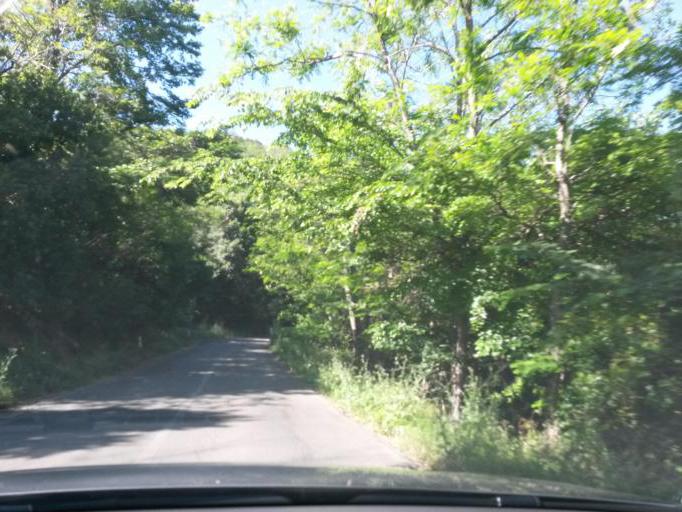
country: IT
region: Tuscany
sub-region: Provincia di Livorno
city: Marciana Marina
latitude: 42.7920
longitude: 10.1856
